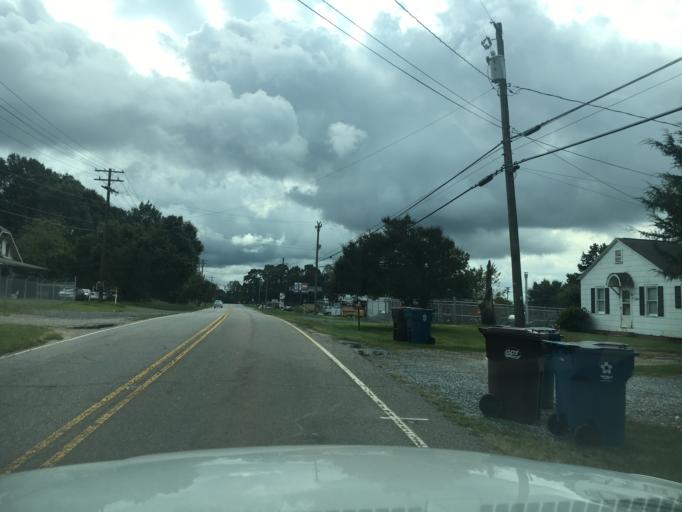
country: US
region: North Carolina
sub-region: Catawba County
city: Saint Stephens
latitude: 35.7237
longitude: -81.2657
